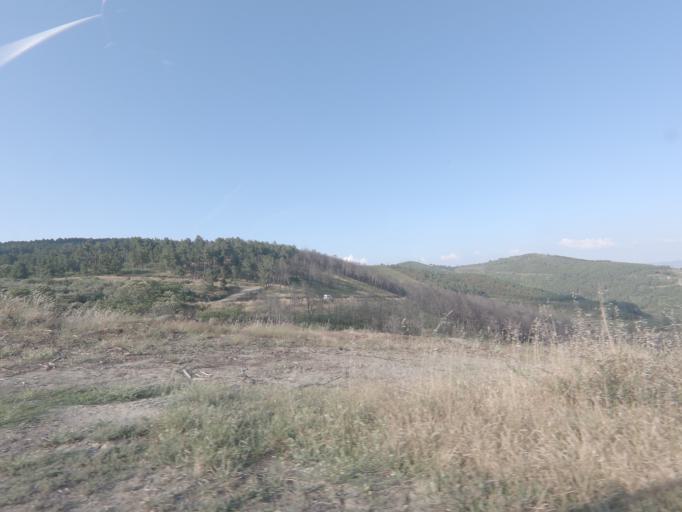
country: PT
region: Vila Real
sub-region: Sabrosa
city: Vilela
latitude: 41.2218
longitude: -7.5995
